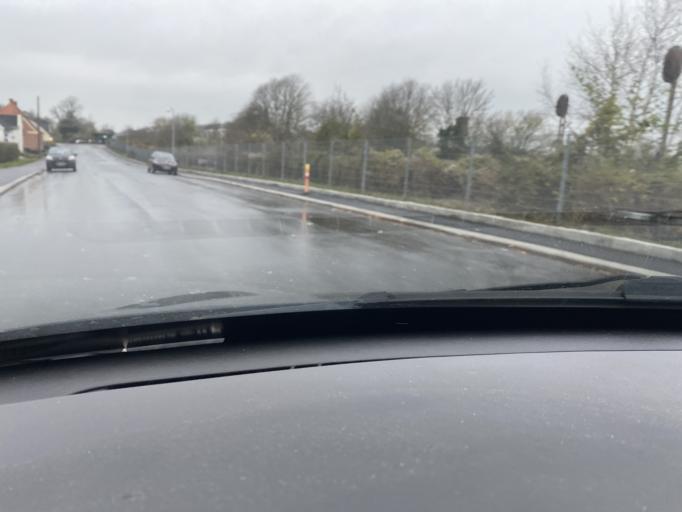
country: DK
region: Zealand
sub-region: Kalundborg Kommune
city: Svebolle
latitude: 55.6514
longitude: 11.2945
